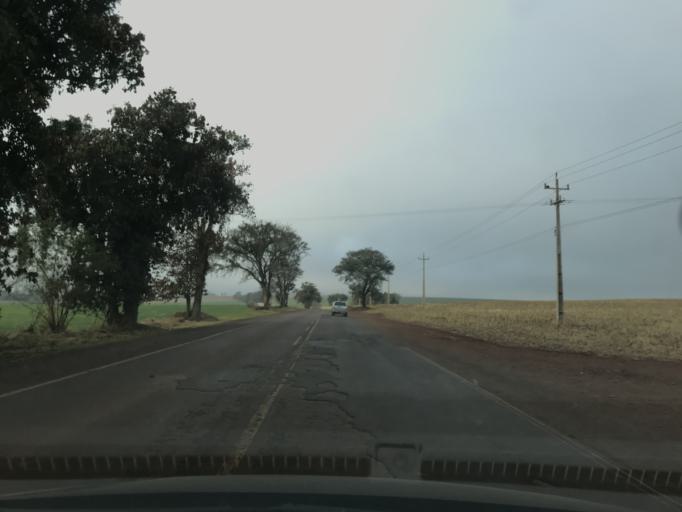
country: BR
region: Parana
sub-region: Toledo
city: Toledo
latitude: -24.6477
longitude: -53.7074
